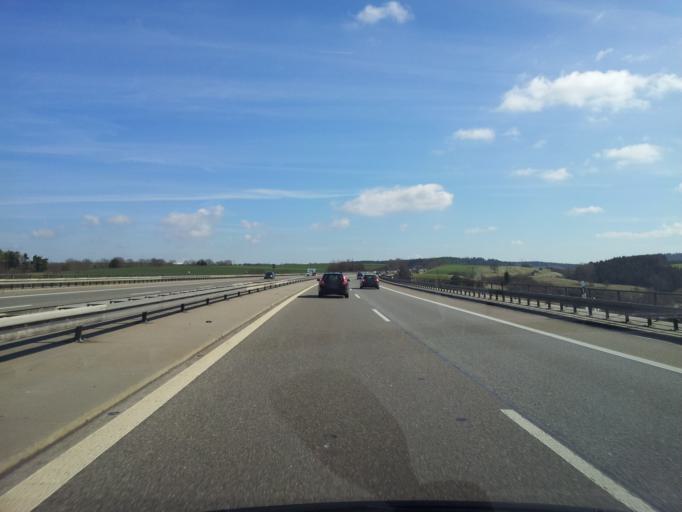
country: DE
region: Baden-Wuerttemberg
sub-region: Freiburg Region
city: Muhlheim am Bach
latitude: 48.3749
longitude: 8.7011
